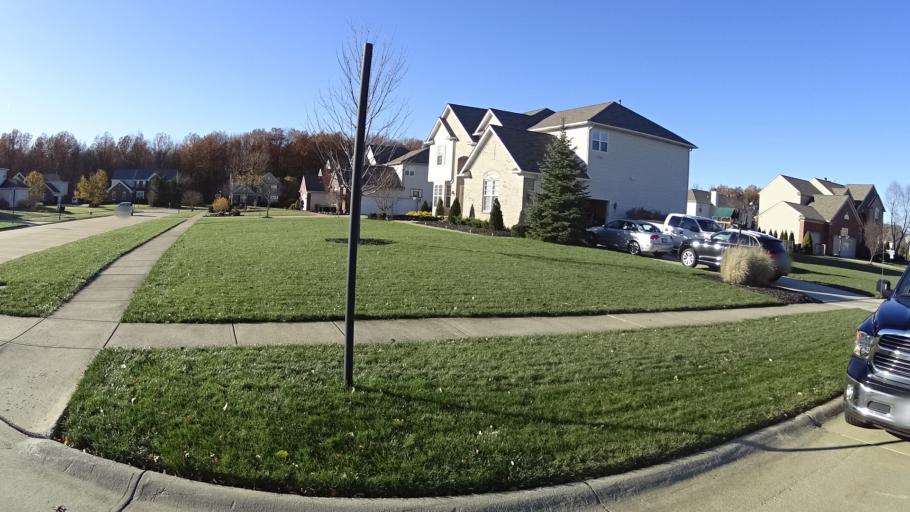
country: US
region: Ohio
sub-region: Lorain County
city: Avon Center
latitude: 41.4482
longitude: -82.0096
